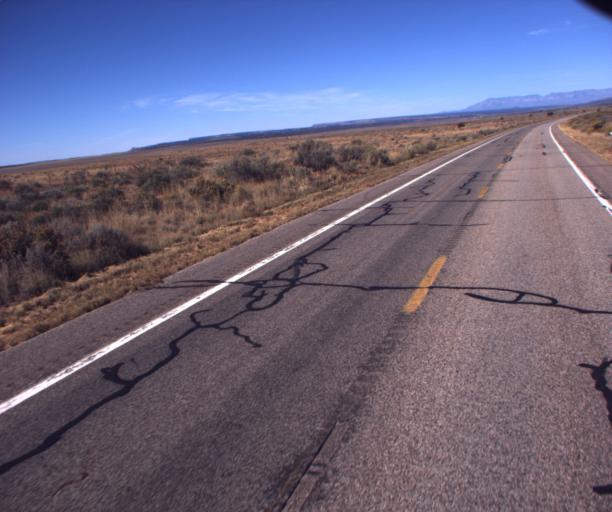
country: US
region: Arizona
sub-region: Mohave County
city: Colorado City
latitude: 36.8885
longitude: -112.9087
